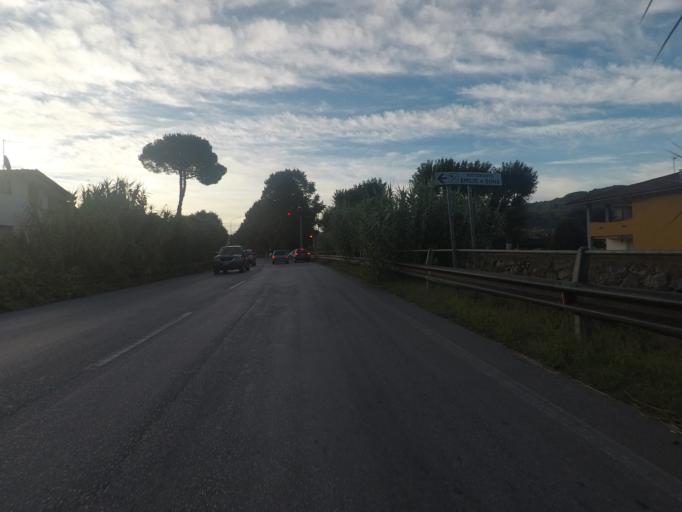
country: IT
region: Tuscany
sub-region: Provincia di Lucca
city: Corsanico-Bargecchia
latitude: 43.9345
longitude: 10.3062
